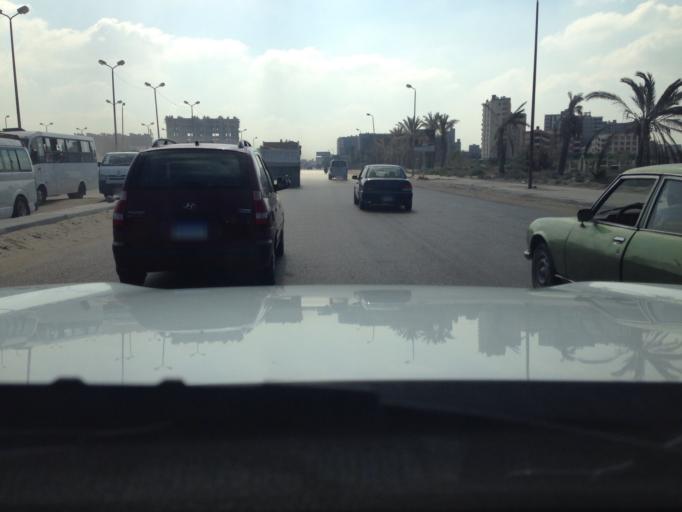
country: EG
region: Alexandria
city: Alexandria
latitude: 31.2039
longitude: 29.9754
